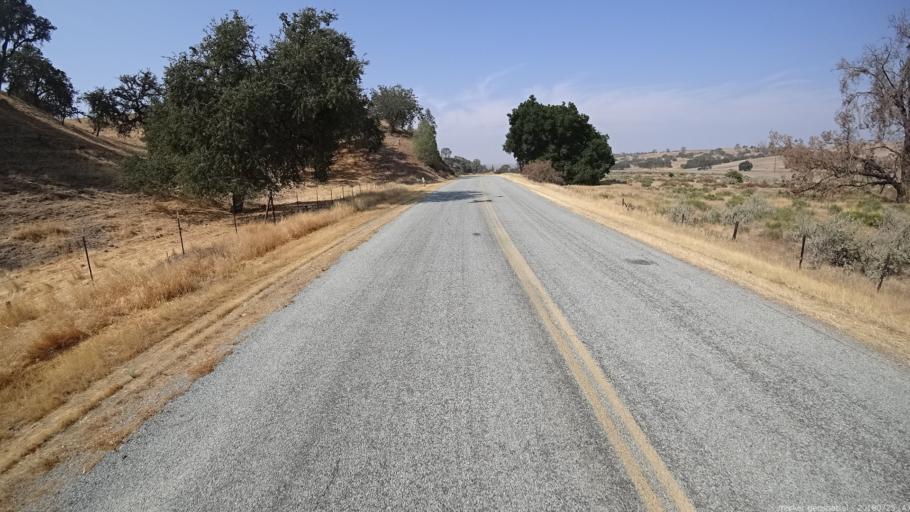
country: US
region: California
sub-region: San Luis Obispo County
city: San Miguel
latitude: 35.8396
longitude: -120.6213
